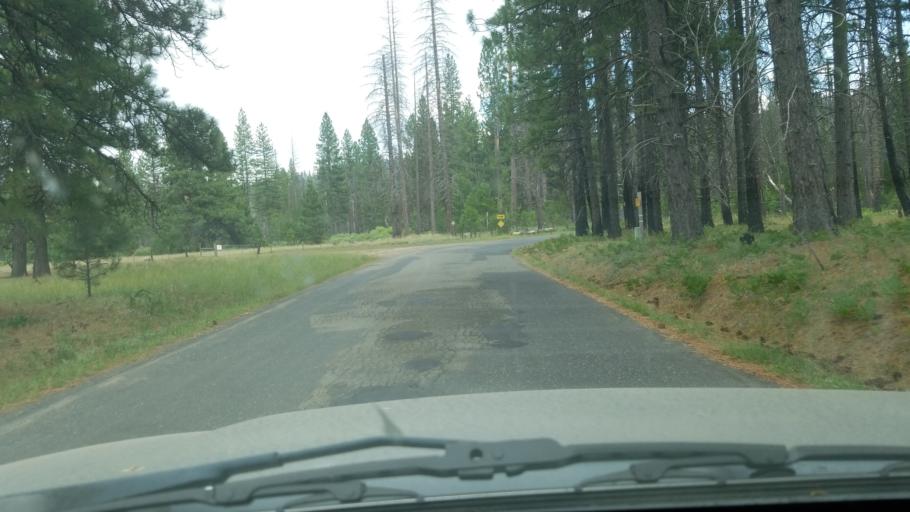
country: US
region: California
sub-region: Mariposa County
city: Yosemite Valley
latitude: 37.8359
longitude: -119.8475
